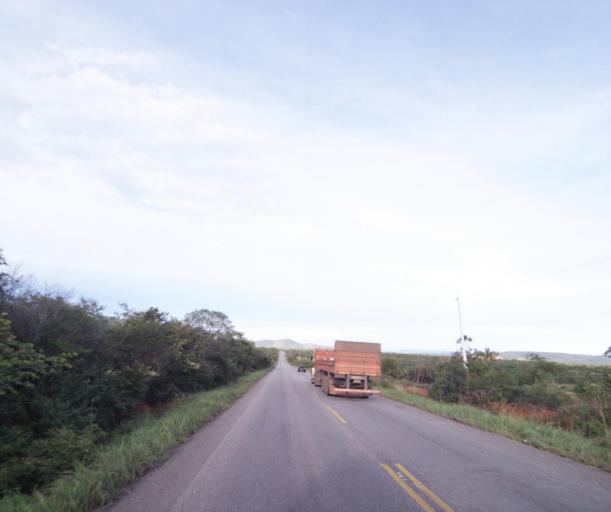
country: BR
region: Bahia
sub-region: Caetite
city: Caetite
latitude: -14.1715
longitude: -42.2766
